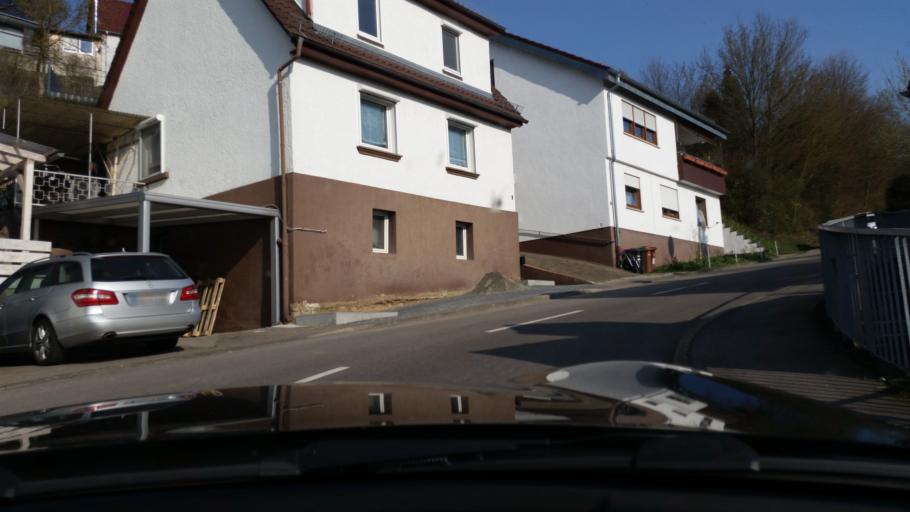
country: DE
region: Baden-Wuerttemberg
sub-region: Regierungsbezirk Stuttgart
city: Mockmuhl
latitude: 49.3266
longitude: 9.3581
